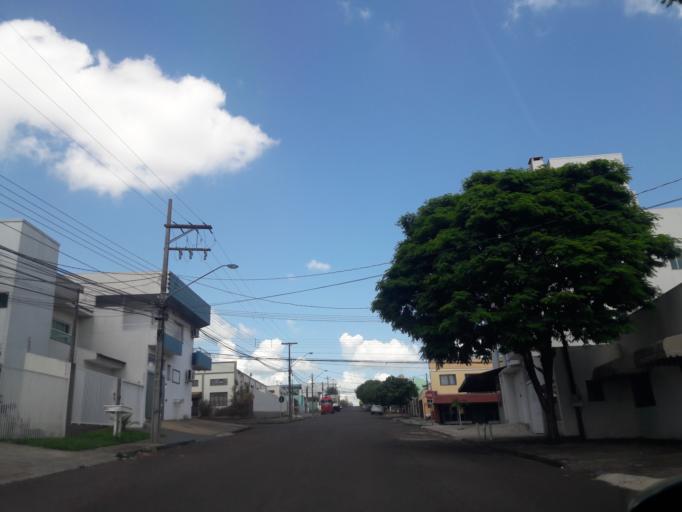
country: BR
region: Parana
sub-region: Cascavel
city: Cascavel
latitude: -24.9724
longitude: -53.4581
